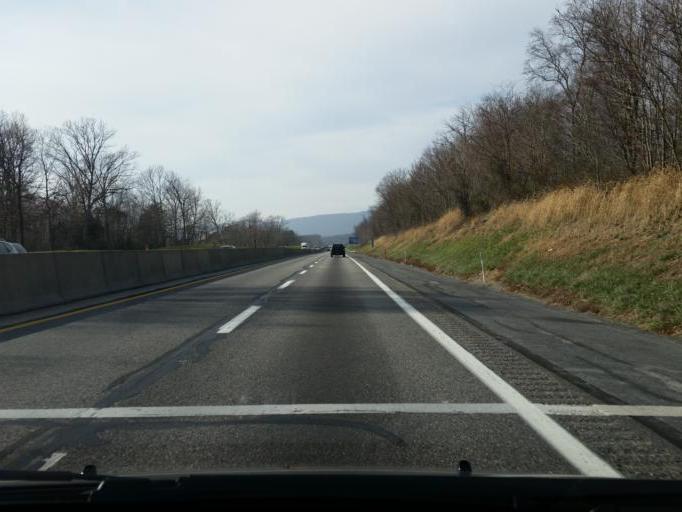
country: US
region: Pennsylvania
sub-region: Cumberland County
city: Shippensburg
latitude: 40.1680
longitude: -77.5815
